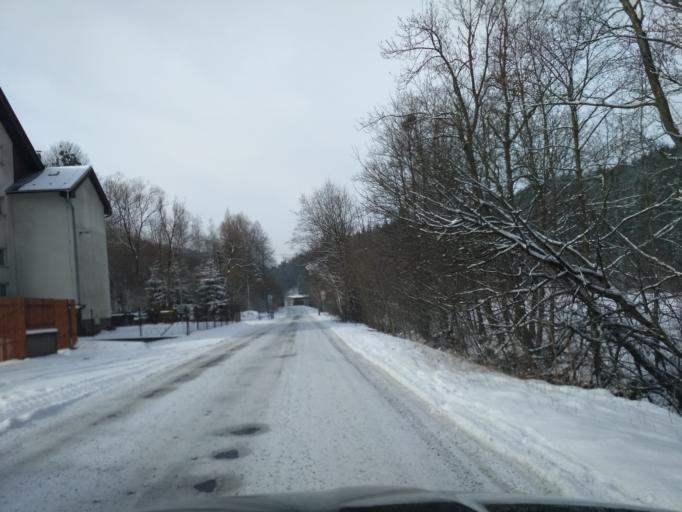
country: CZ
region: Zlin
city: Valasska Bystrice
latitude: 49.4091
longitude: 18.1248
